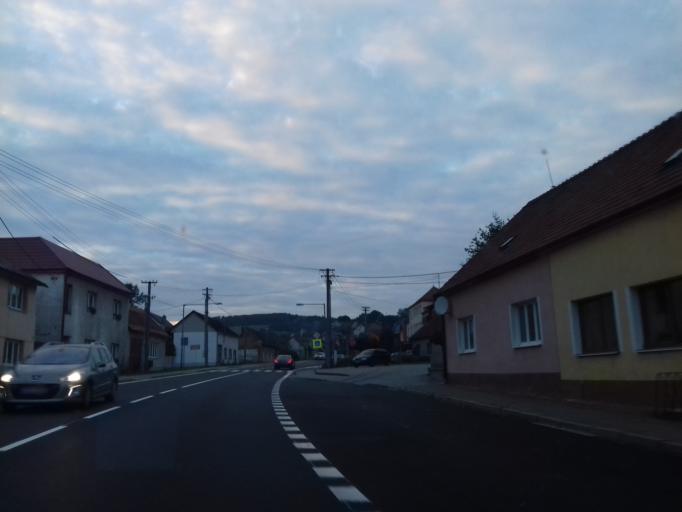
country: CZ
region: Zlin
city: Bojkovice
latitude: 48.9654
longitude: 17.8633
